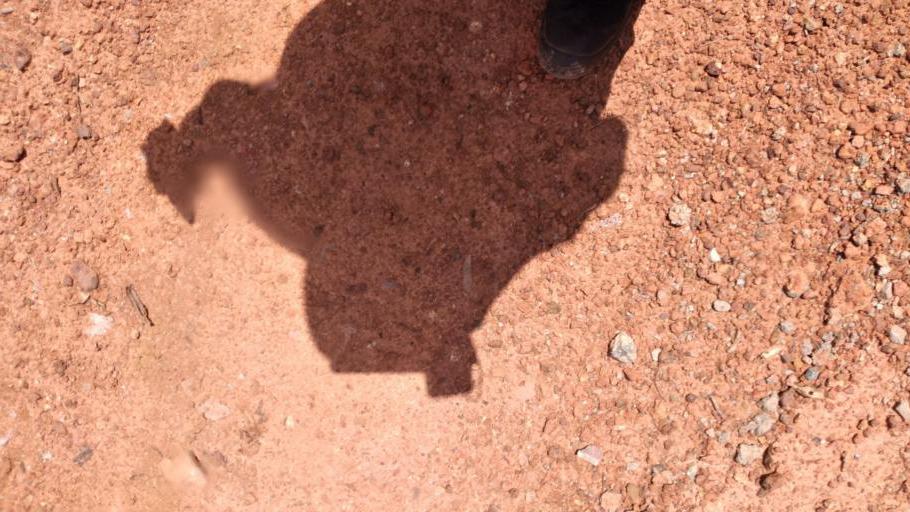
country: ML
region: Koulikoro
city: Kangaba
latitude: 12.0721
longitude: -8.5372
